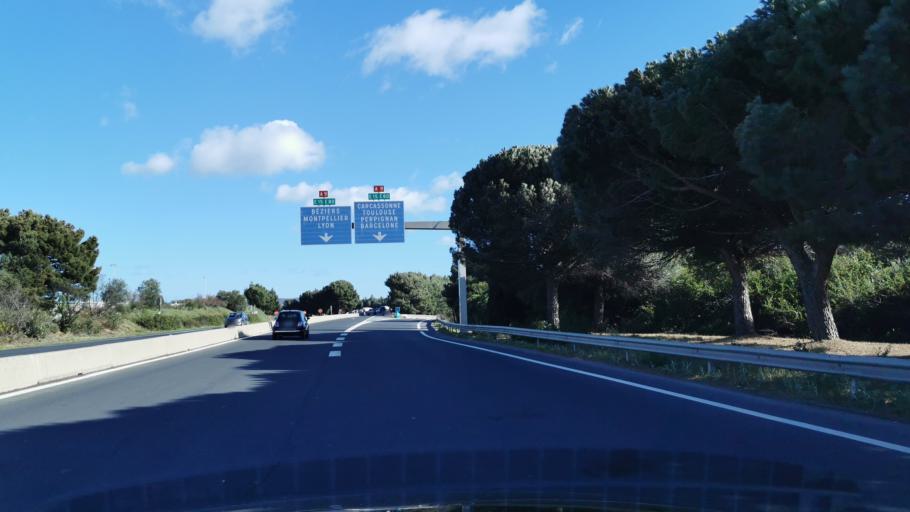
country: FR
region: Languedoc-Roussillon
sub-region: Departement de l'Aude
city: Narbonne
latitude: 43.1642
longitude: 2.9907
